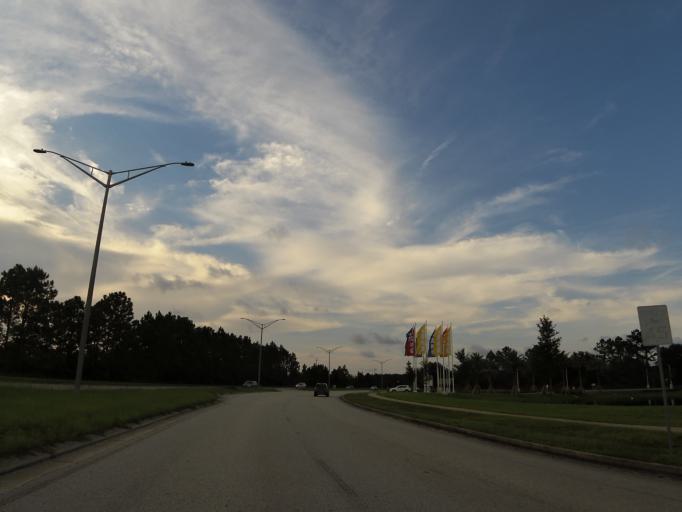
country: US
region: Florida
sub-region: Saint Johns County
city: Ponte Vedra Beach
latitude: 30.2371
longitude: -81.5192
